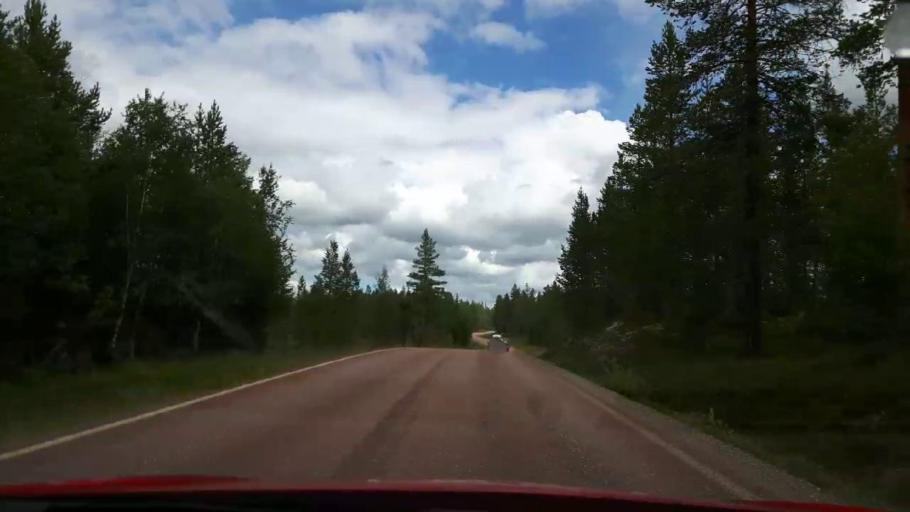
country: NO
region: Hedmark
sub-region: Trysil
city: Innbygda
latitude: 61.8983
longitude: 12.9885
